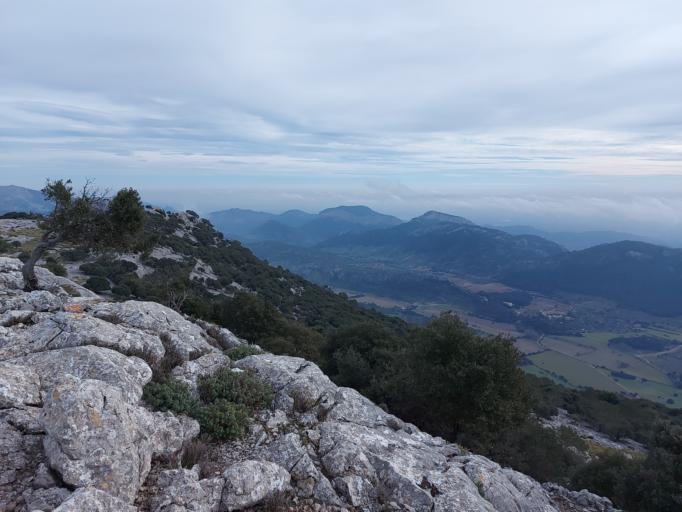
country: ES
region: Balearic Islands
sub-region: Illes Balears
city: Soller
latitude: 39.7443
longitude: 2.7351
